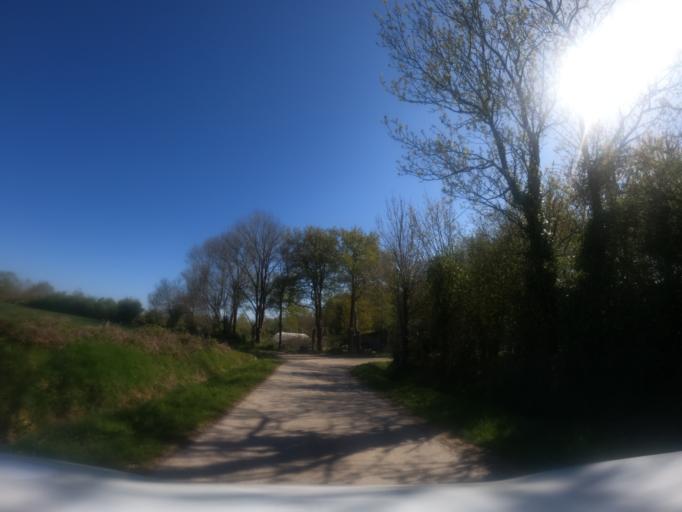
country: FR
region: Pays de la Loire
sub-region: Departement de la Vendee
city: Le Champ-Saint-Pere
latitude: 46.5360
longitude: -1.3393
